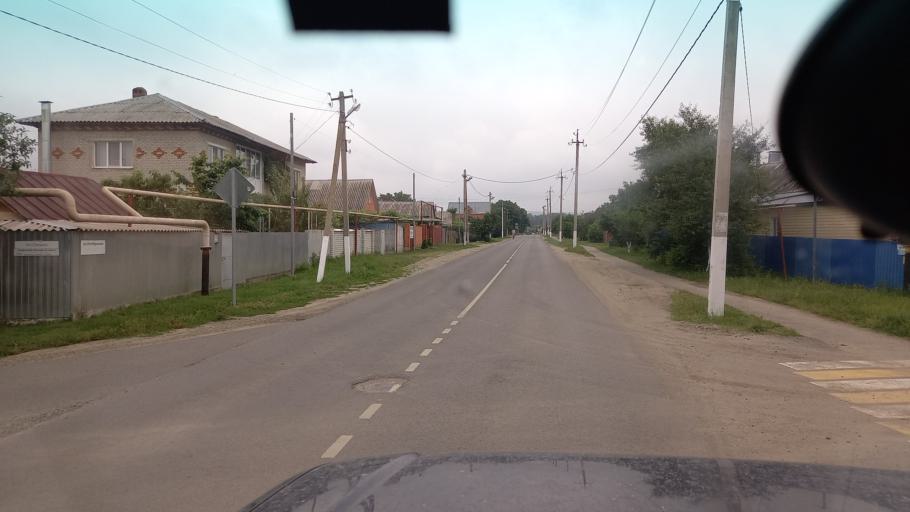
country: RU
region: Krasnodarskiy
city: Mostovskoy
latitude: 44.4148
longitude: 40.7925
